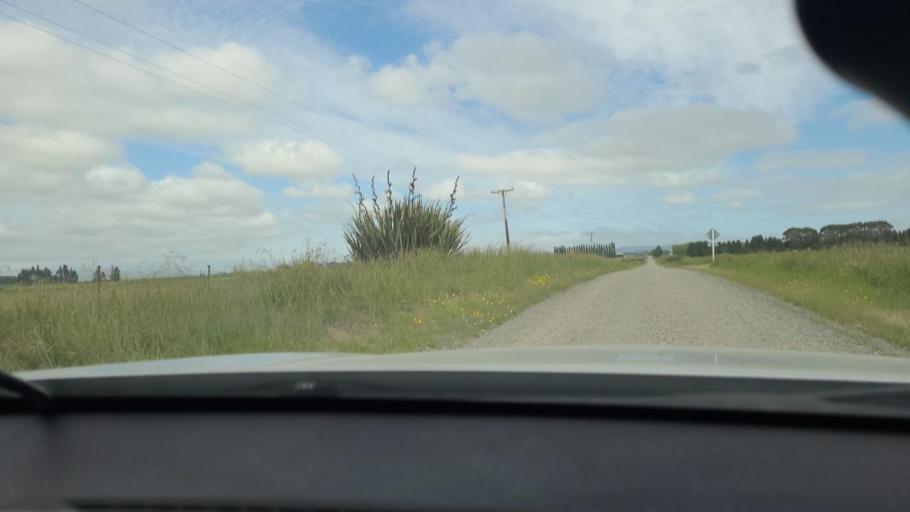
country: NZ
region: Southland
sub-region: Southland District
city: Winton
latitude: -45.9788
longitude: 168.1093
